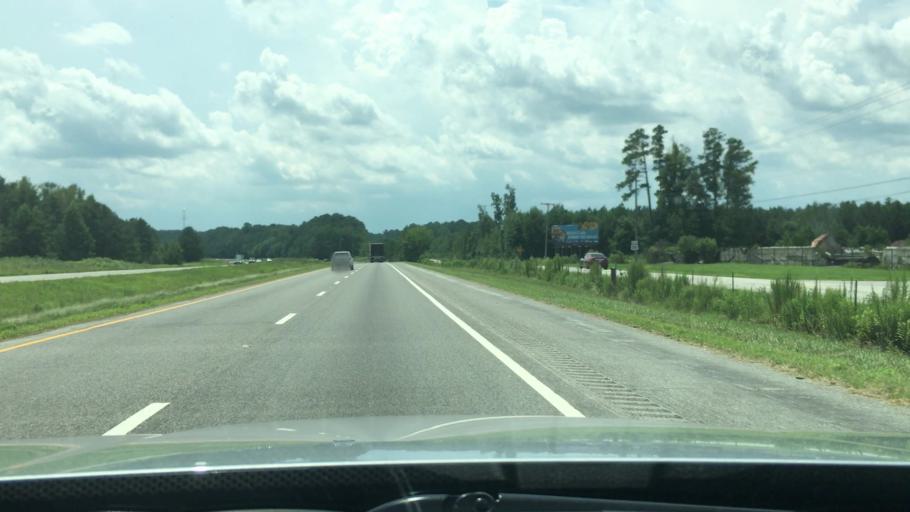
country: US
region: Virginia
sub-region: City of Emporia
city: Emporia
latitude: 36.8298
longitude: -77.4506
